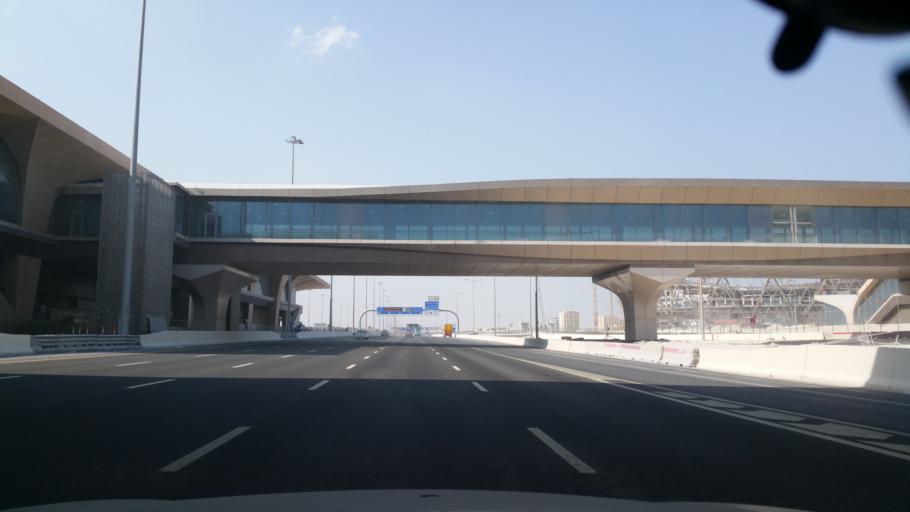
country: QA
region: Baladiyat Umm Salal
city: Umm Salal Muhammad
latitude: 25.4140
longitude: 51.4884
